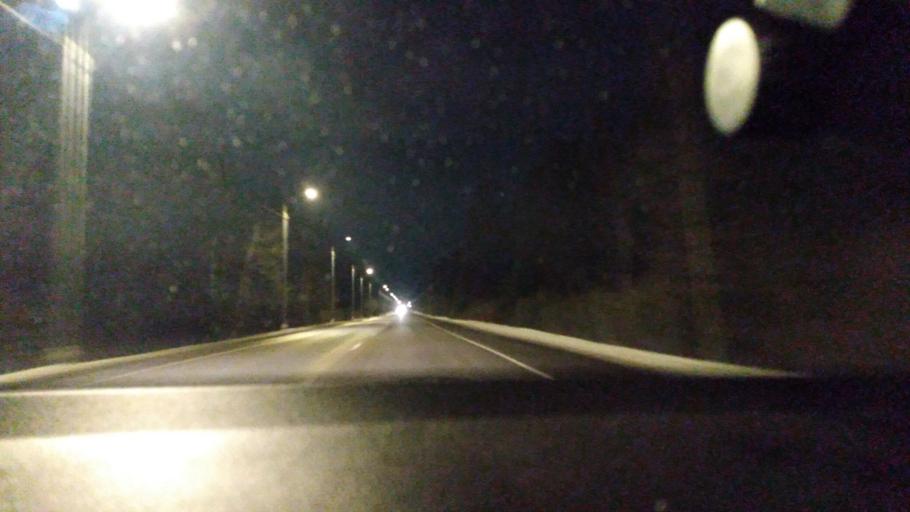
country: RU
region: Moskovskaya
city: Yegor'yevsk
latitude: 55.4554
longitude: 38.9941
